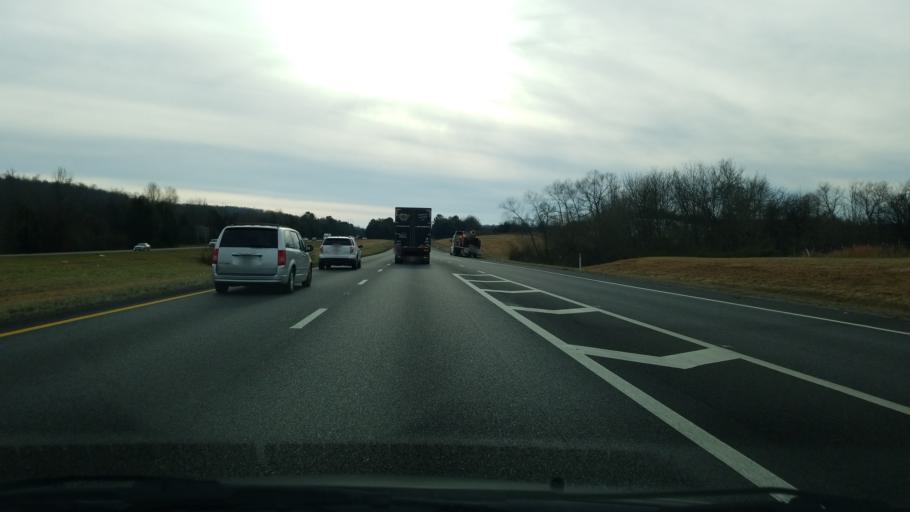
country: US
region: Tennessee
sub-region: Monroe County
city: Sweetwater
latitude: 35.5958
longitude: -84.5194
